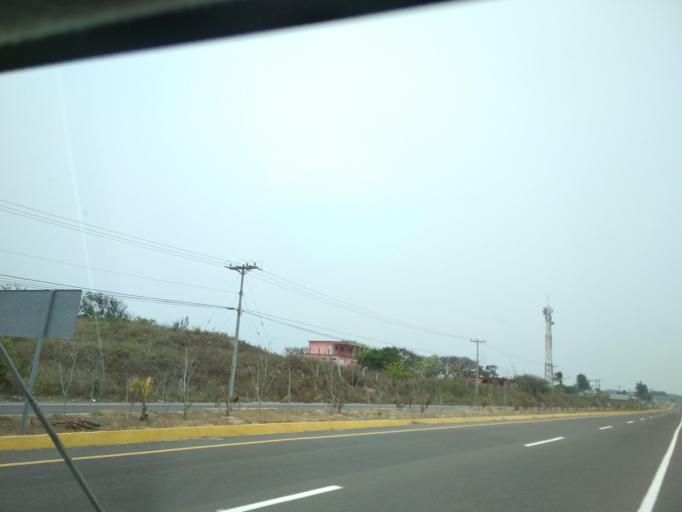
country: MX
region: Veracruz
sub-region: Alvarado
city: Playa de la Libertad
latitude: 19.0559
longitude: -96.0529
